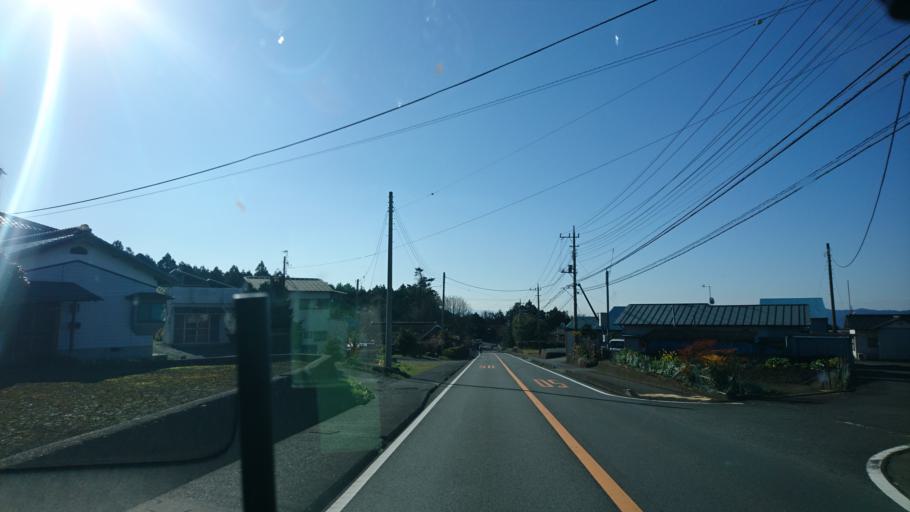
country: JP
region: Shizuoka
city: Fujinomiya
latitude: 35.2889
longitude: 138.6021
